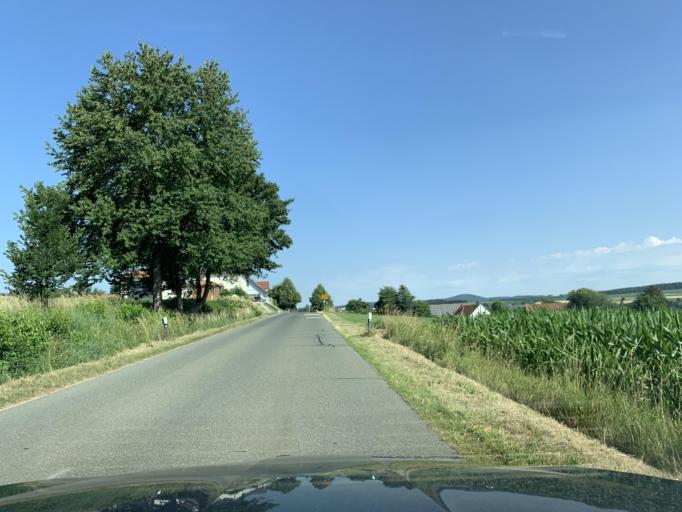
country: DE
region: Bavaria
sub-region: Upper Palatinate
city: Schwarzhofen
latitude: 49.3824
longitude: 12.3297
